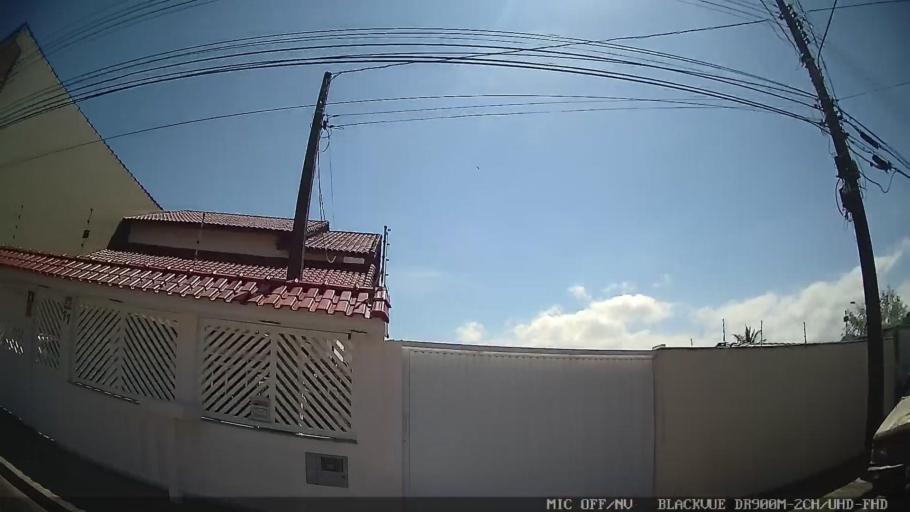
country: BR
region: Sao Paulo
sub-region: Peruibe
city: Peruibe
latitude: -24.3196
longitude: -47.0047
